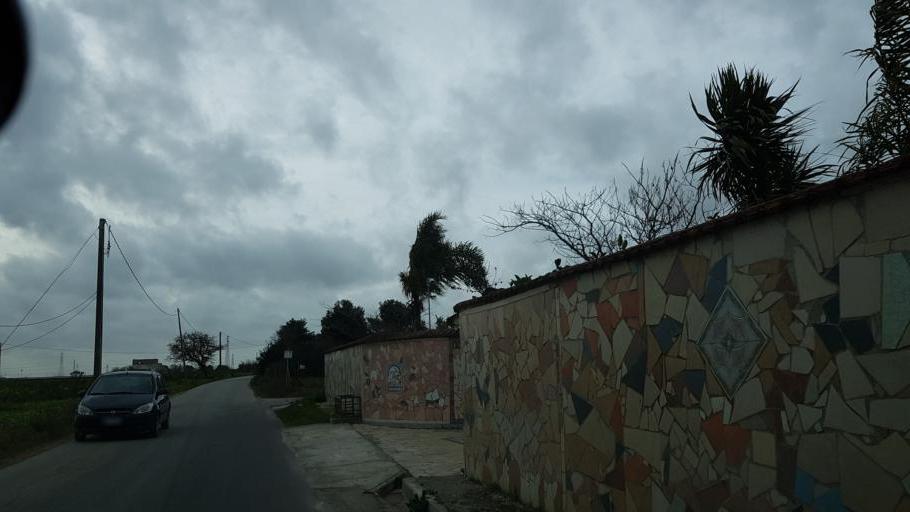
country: IT
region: Apulia
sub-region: Provincia di Brindisi
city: Brindisi
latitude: 40.6134
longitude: 17.9272
